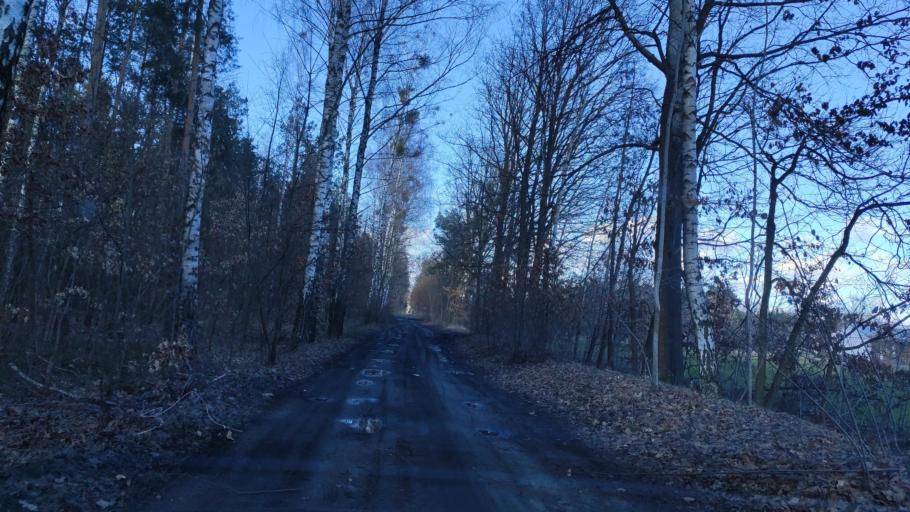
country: PL
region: Masovian Voivodeship
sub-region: Powiat radomski
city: Jedlnia-Letnisko
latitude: 51.4603
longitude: 21.3248
